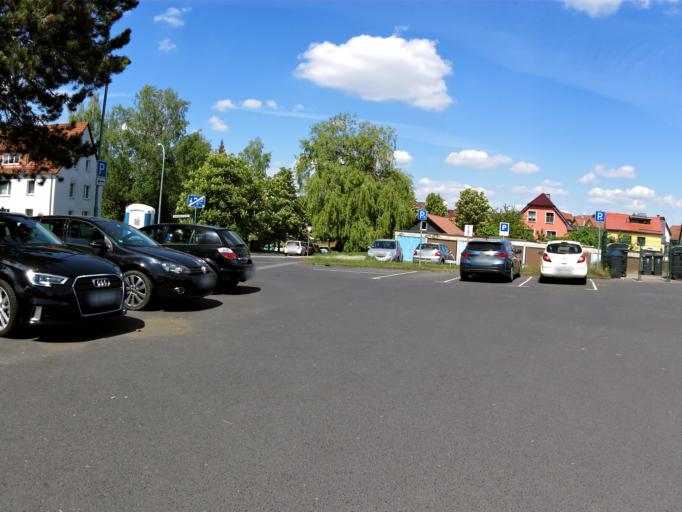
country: DE
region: Thuringia
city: Bad Salzungen
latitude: 50.8089
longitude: 10.2262
